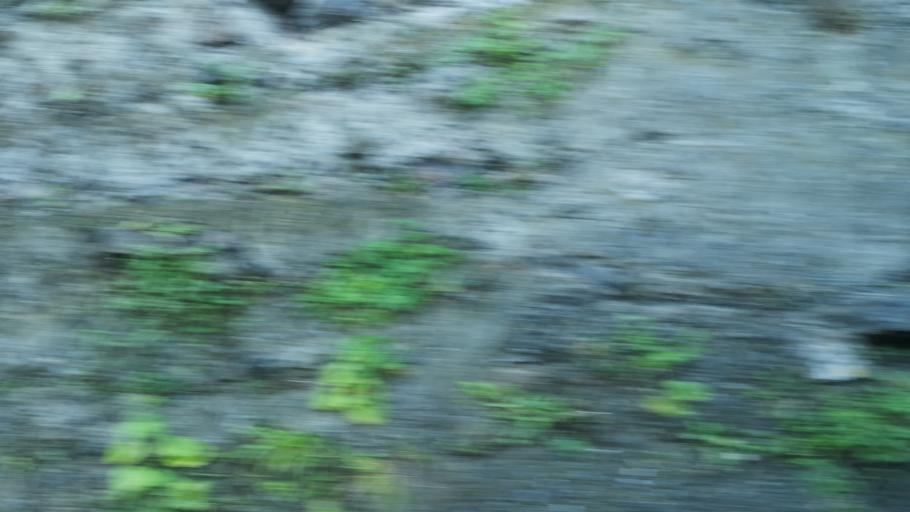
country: ES
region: Canary Islands
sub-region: Provincia de Santa Cruz de Tenerife
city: Hermigua
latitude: 28.1327
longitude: -17.1988
